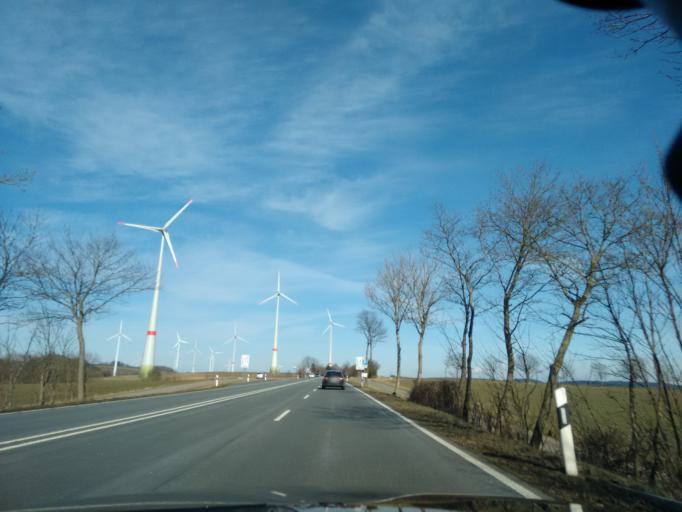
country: DE
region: North Rhine-Westphalia
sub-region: Regierungsbezirk Detmold
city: Altenbeken
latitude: 51.7296
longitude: 8.9161
